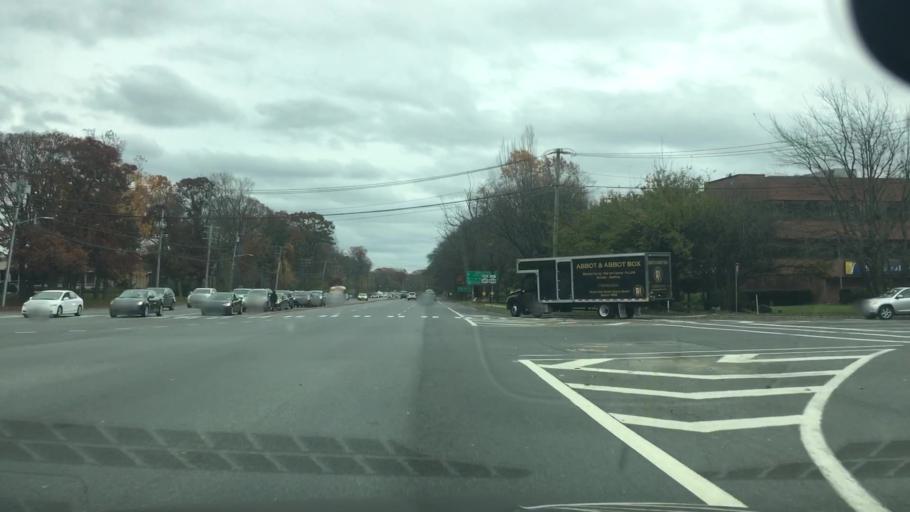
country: US
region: New York
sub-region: Suffolk County
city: Hauppauge
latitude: 40.8251
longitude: -73.2350
